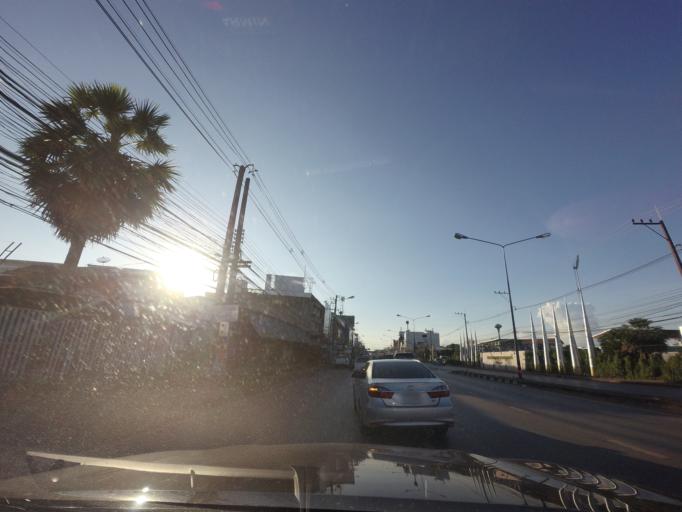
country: TH
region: Changwat Udon Thani
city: Udon Thani
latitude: 17.3951
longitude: 102.8108
